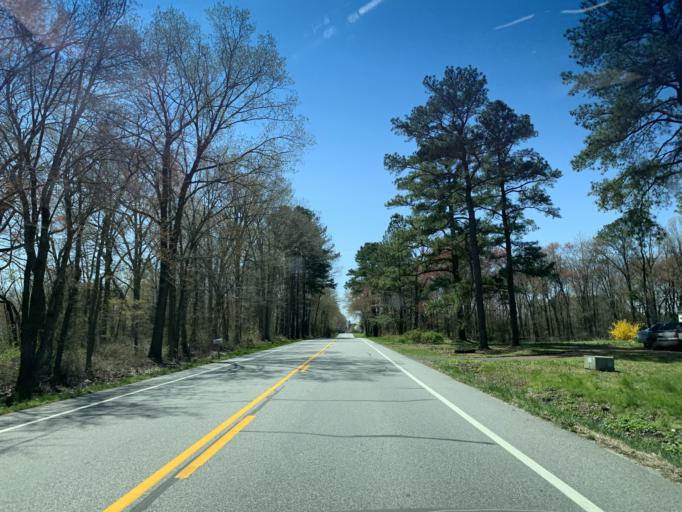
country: US
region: Maryland
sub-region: Talbot County
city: Easton
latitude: 38.8394
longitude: -76.0262
